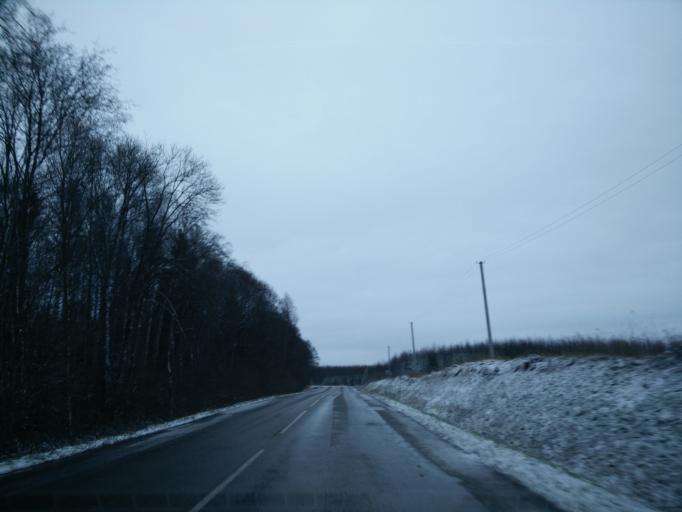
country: LT
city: Tytuveneliai
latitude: 55.5043
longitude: 23.2986
